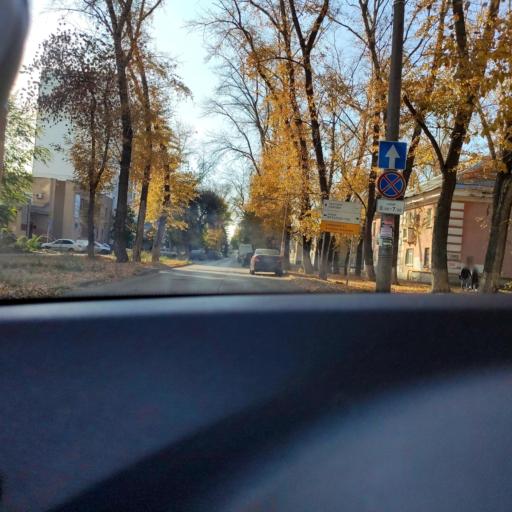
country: RU
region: Samara
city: Petra-Dubrava
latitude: 53.2269
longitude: 50.2700
